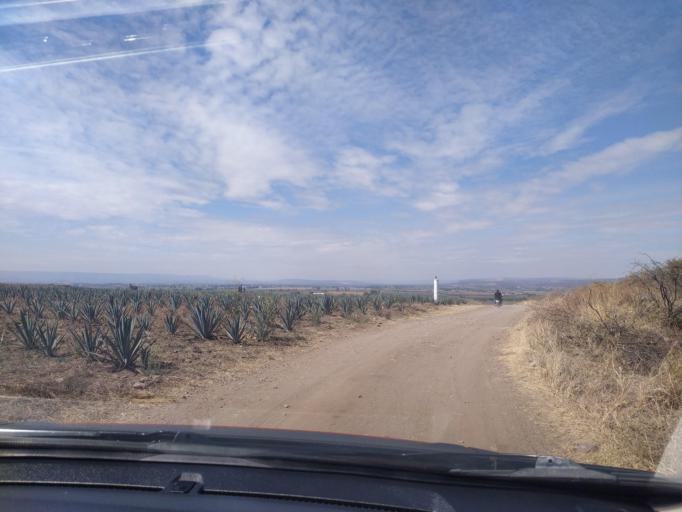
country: MX
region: Guanajuato
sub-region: San Francisco del Rincon
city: San Ignacio de Hidalgo
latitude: 20.8815
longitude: -101.8461
